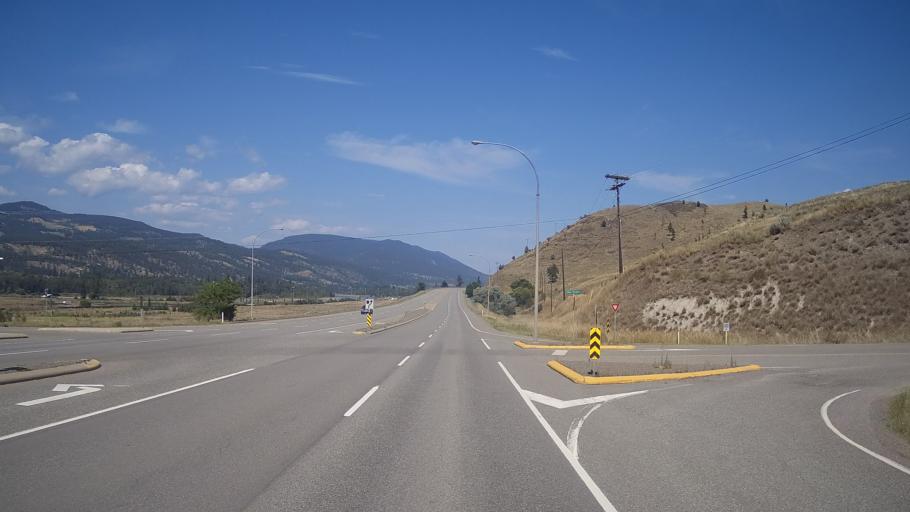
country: CA
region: British Columbia
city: Kamloops
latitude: 50.8194
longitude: -120.2917
